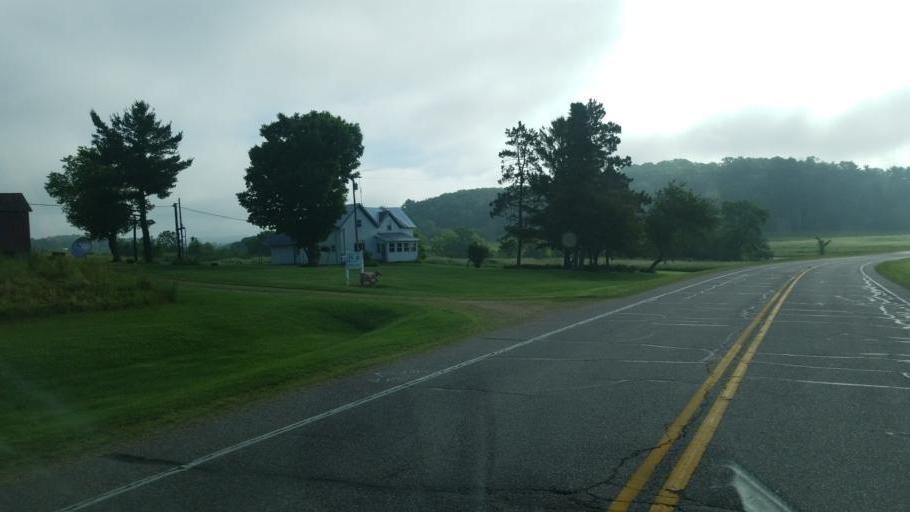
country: US
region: Wisconsin
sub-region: Juneau County
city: Elroy
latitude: 43.6731
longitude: -90.2428
